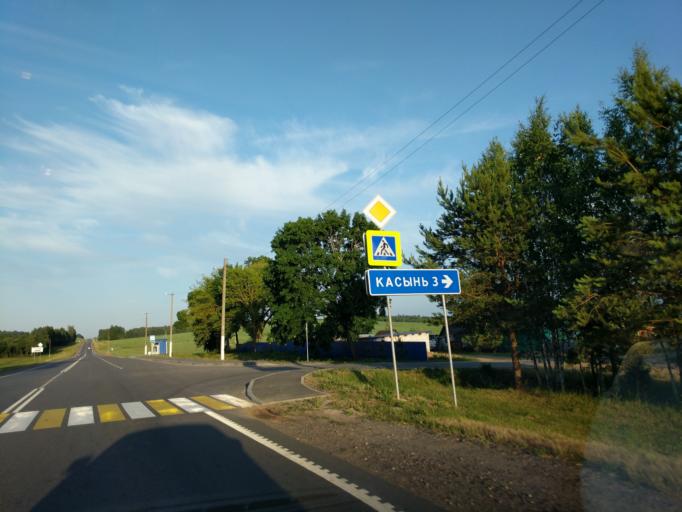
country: BY
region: Minsk
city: Syomkava
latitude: 54.0964
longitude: 27.5019
